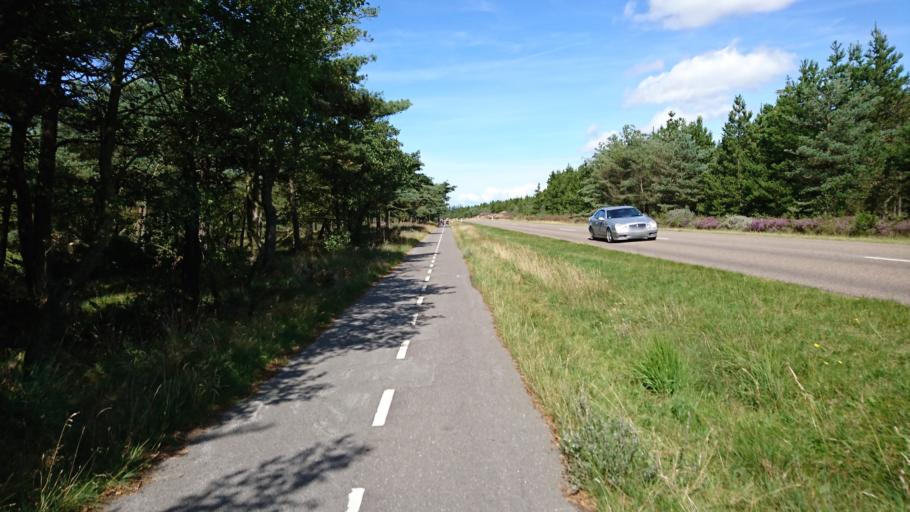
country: DK
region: South Denmark
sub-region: Fano Kommune
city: Nordby
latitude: 55.4025
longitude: 8.4203
